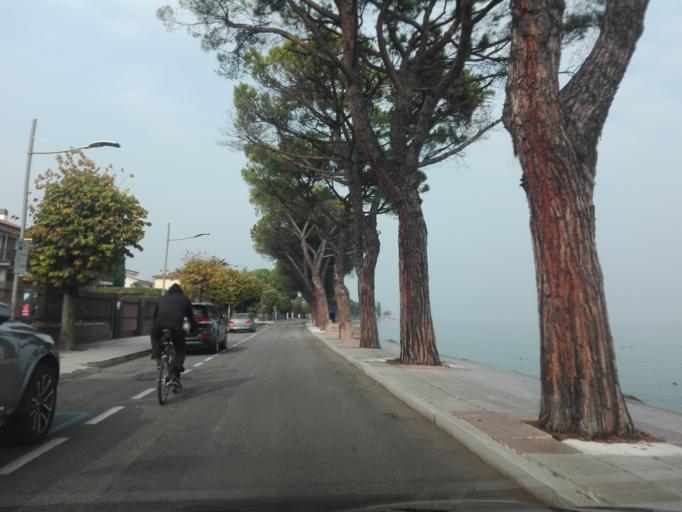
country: IT
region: Veneto
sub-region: Provincia di Verona
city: Peschiera del Garda
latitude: 45.4410
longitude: 10.6886
